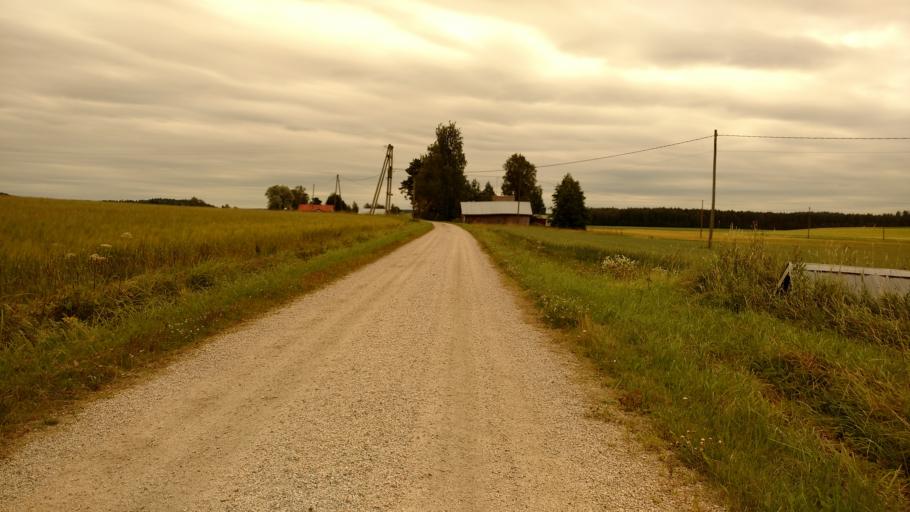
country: FI
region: Varsinais-Suomi
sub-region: Turku
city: Paimio
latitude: 60.4167
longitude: 22.8391
